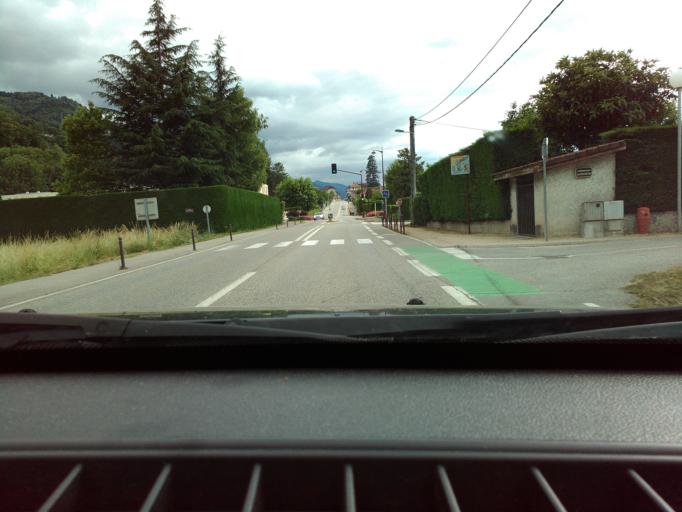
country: FR
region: Rhone-Alpes
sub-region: Departement de l'Isere
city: Froges
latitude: 45.2783
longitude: 5.9292
